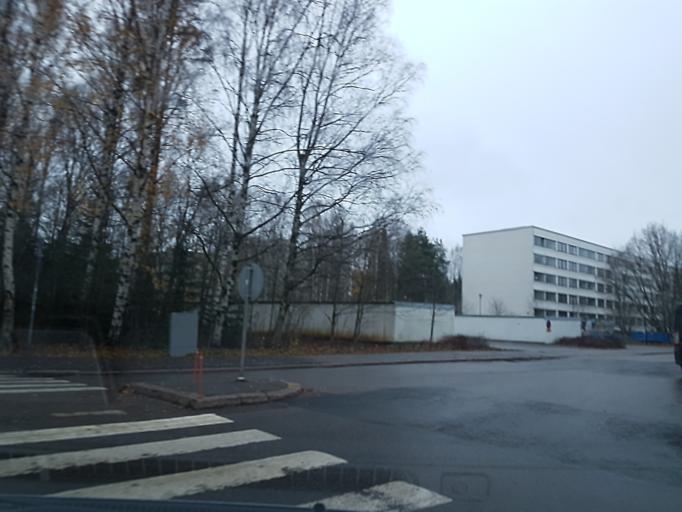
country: FI
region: Uusimaa
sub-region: Helsinki
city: Vantaa
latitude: 60.2306
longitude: 25.0864
